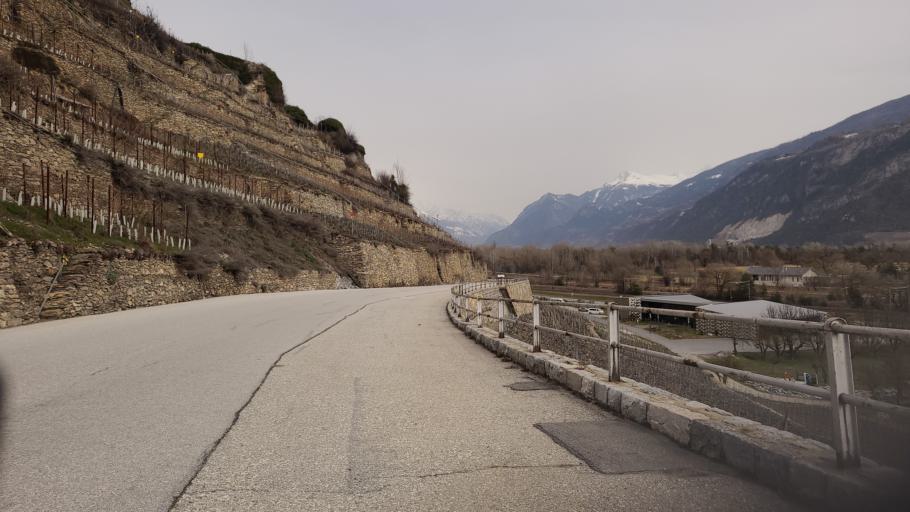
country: CH
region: Valais
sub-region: Sion District
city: Sitten
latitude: 46.2417
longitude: 7.3741
